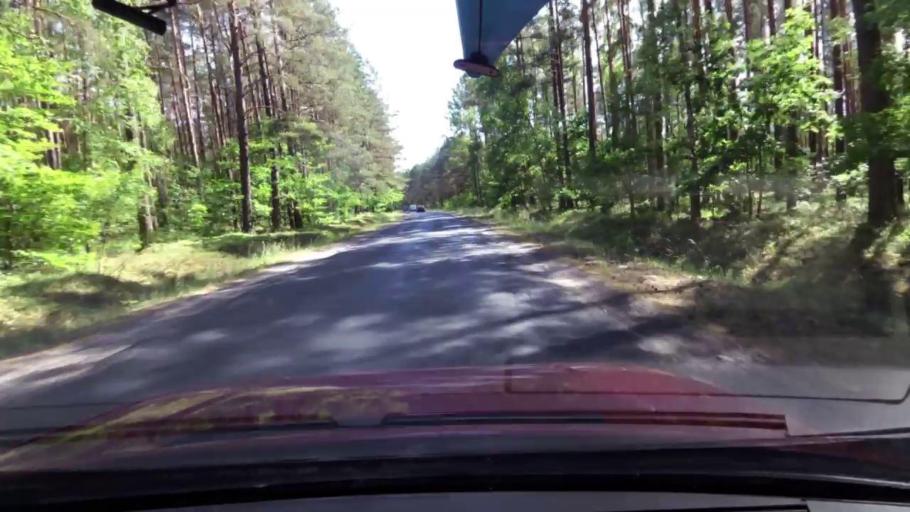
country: PL
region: Pomeranian Voivodeship
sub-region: Powiat slupski
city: Kepice
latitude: 54.3132
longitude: 16.9615
